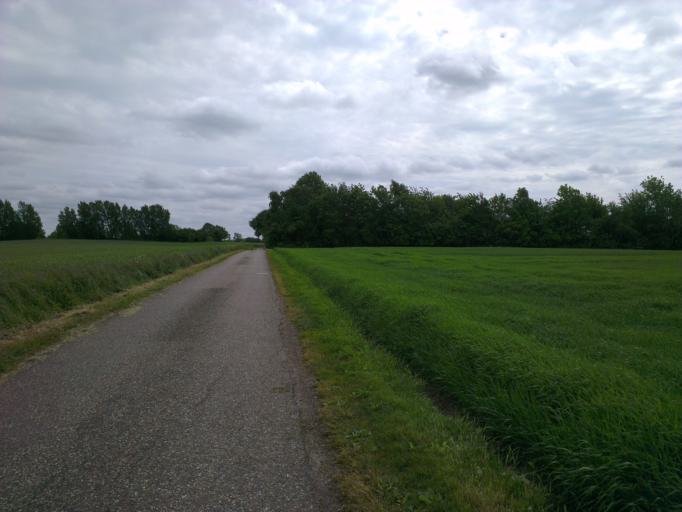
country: DK
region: Capital Region
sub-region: Frederikssund Kommune
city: Frederikssund
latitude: 55.8090
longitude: 12.0766
